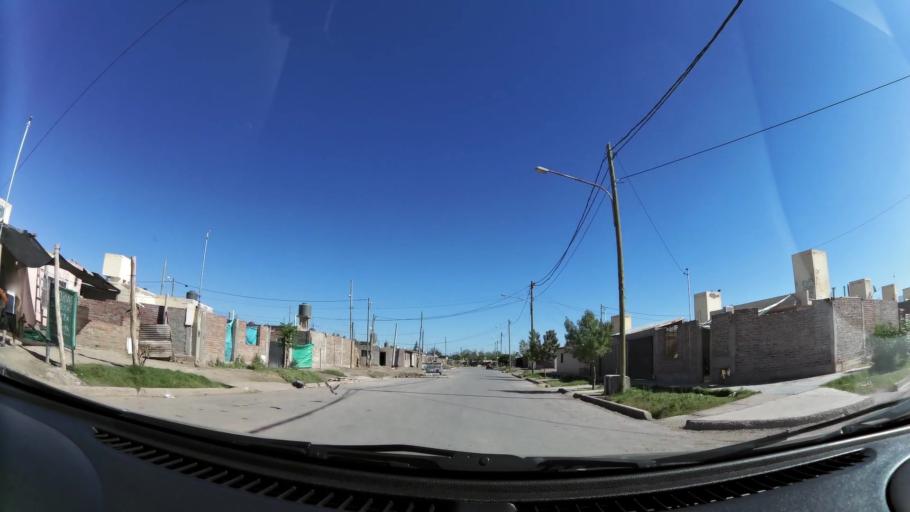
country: AR
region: Mendoza
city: Las Heras
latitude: -32.8335
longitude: -68.8177
